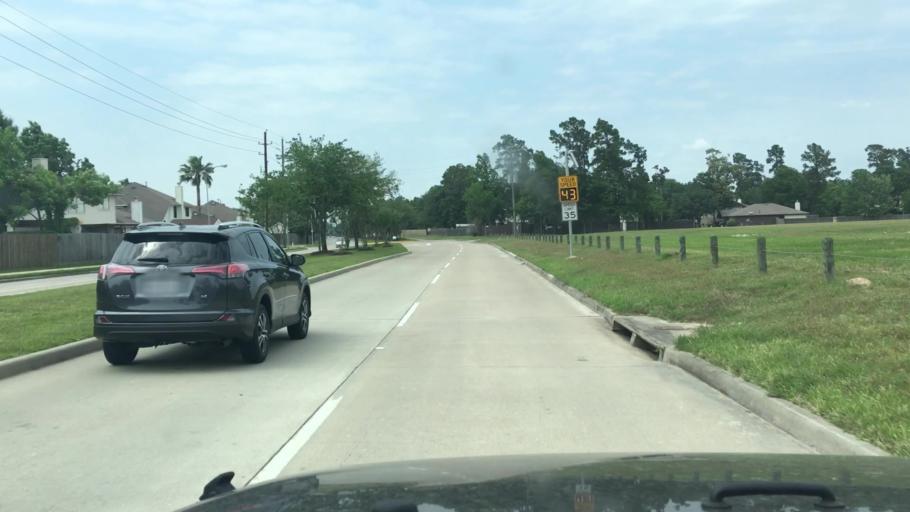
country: US
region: Texas
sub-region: Harris County
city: Atascocita
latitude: 29.9636
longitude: -95.2102
